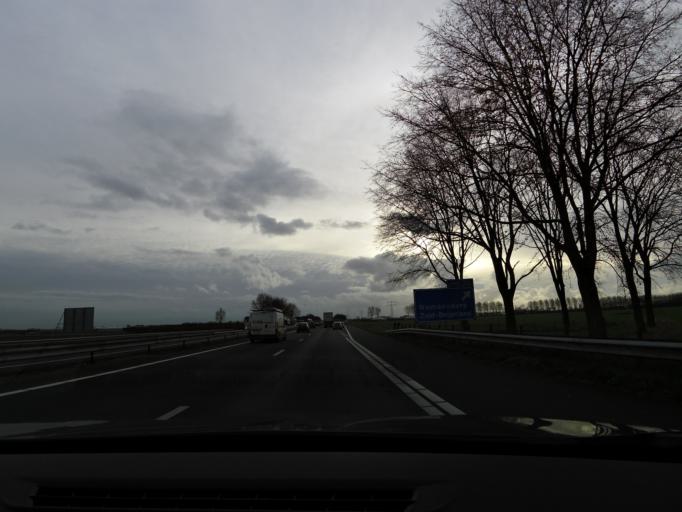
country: NL
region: South Holland
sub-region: Gemeente Oud-Beijerland
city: Oud-Beijerland
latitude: 51.7581
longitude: 4.4179
